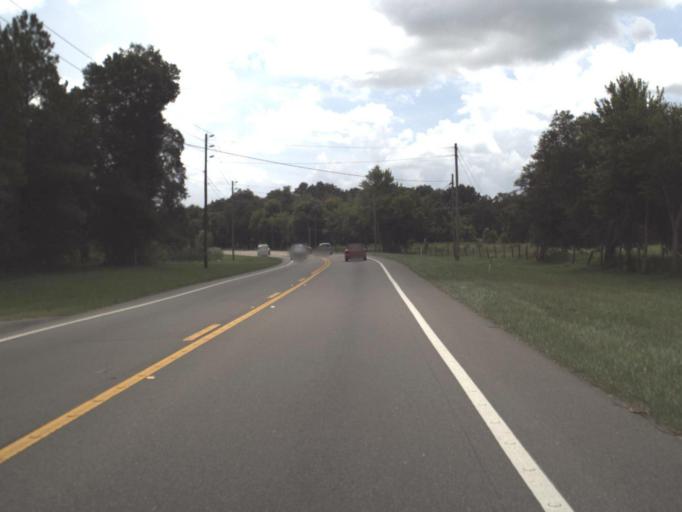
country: US
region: Florida
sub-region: Pasco County
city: Shady Hills
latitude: 28.3251
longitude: -82.5252
